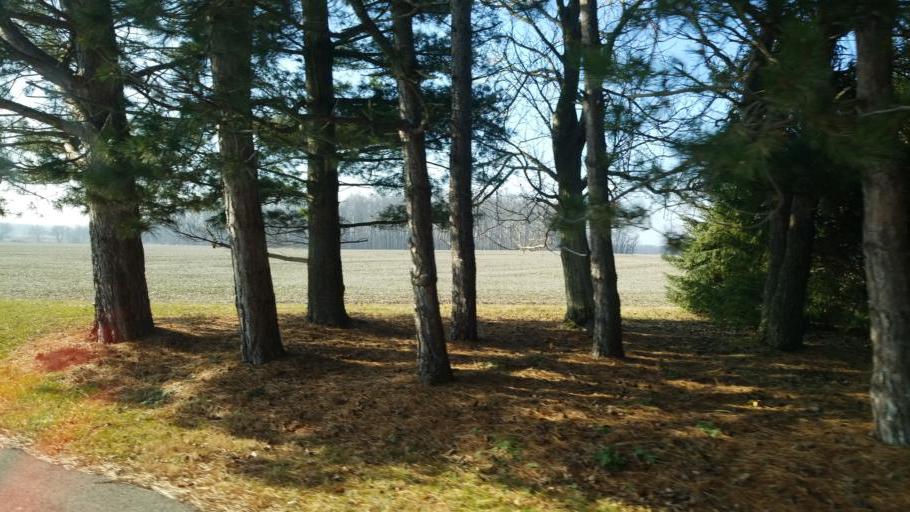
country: US
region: Ohio
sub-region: Seneca County
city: Tiffin
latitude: 41.0768
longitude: -83.1127
